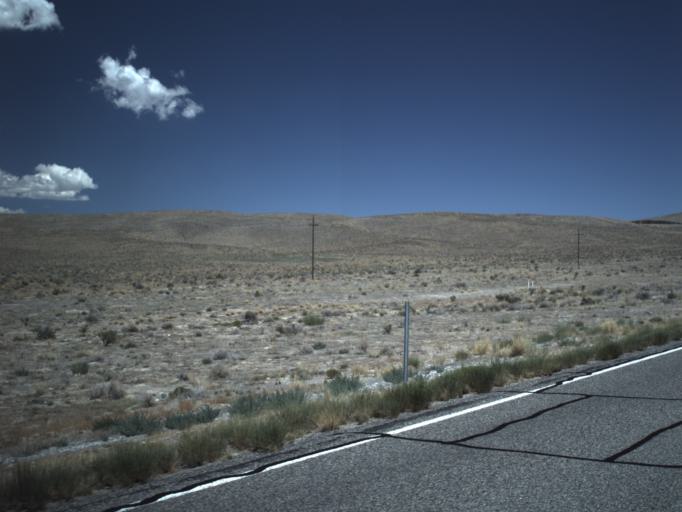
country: US
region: Utah
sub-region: Beaver County
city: Milford
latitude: 39.0251
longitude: -113.3546
